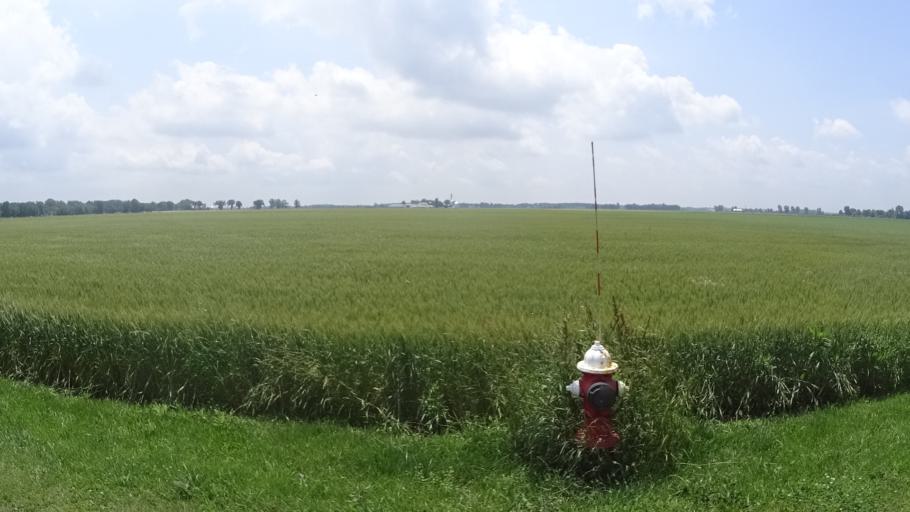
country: US
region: Ohio
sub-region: Huron County
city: Bellevue
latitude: 41.3247
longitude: -82.7630
